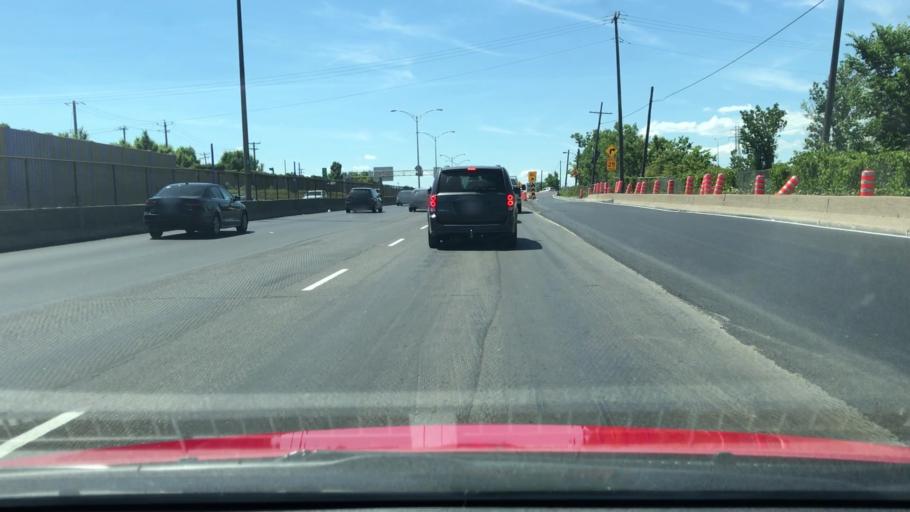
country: CA
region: Quebec
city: Cote-Saint-Luc
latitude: 45.4474
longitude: -73.6759
